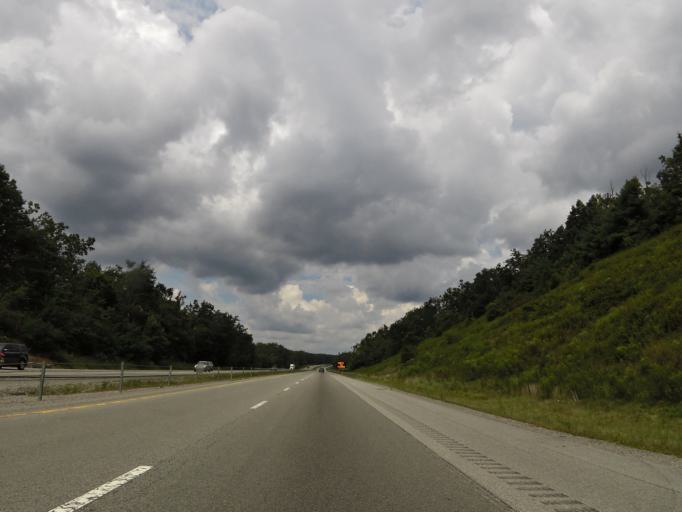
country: US
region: Tennessee
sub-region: Putnam County
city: Monterey
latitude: 36.1137
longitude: -85.2435
